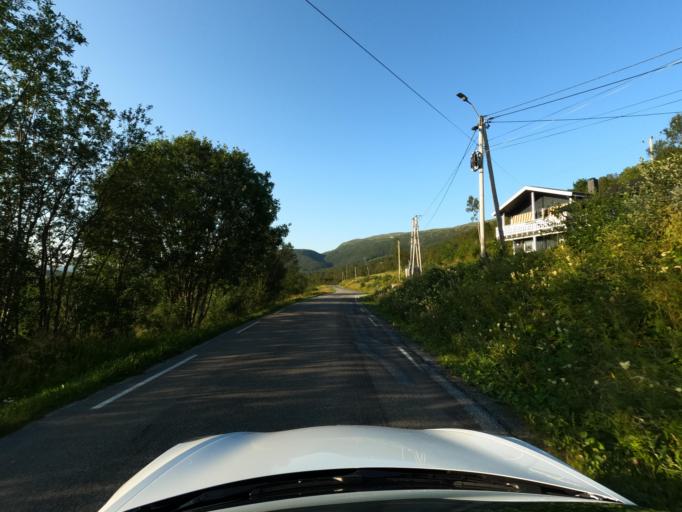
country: NO
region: Nordland
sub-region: Ballangen
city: Ballangen
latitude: 68.5197
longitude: 16.7582
